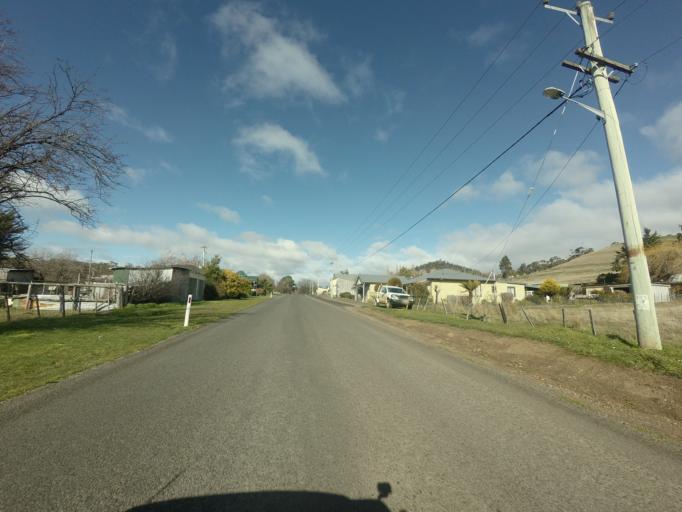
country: AU
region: Tasmania
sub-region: Derwent Valley
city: New Norfolk
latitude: -42.6133
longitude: 146.7135
